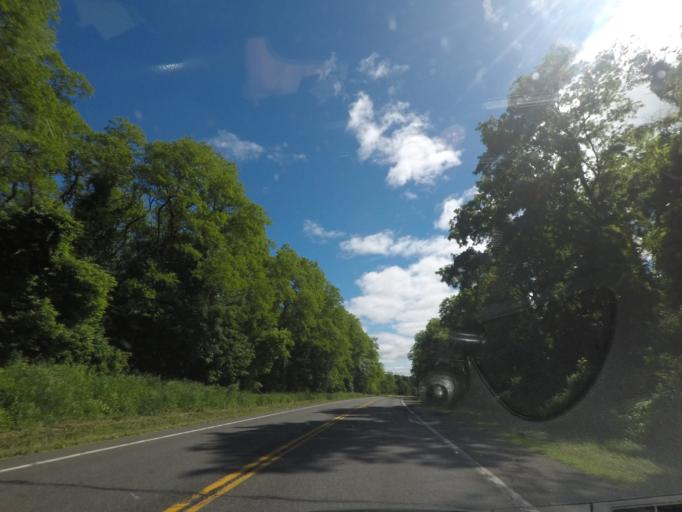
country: US
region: Massachusetts
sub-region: Berkshire County
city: Sheffield
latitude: 42.1213
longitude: -73.5266
